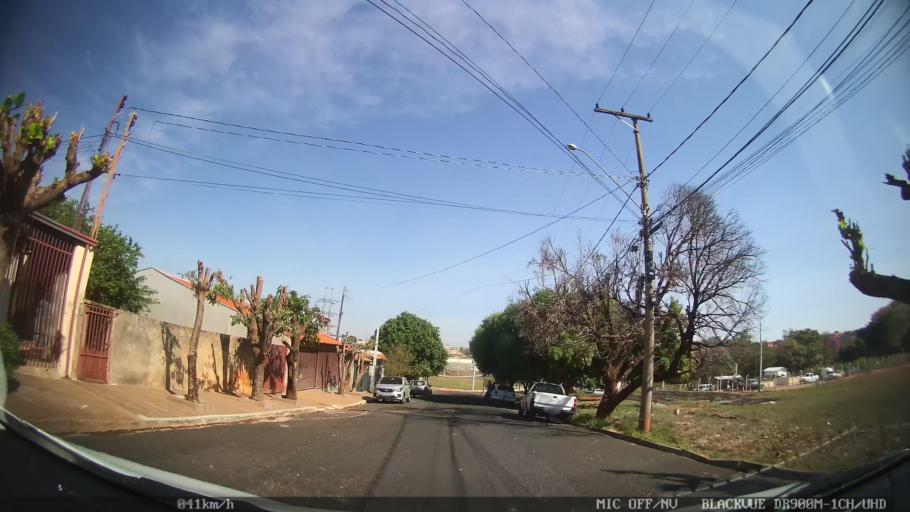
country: BR
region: Sao Paulo
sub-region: Sao Jose Do Rio Preto
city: Sao Jose do Rio Preto
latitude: -20.7878
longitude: -49.4128
